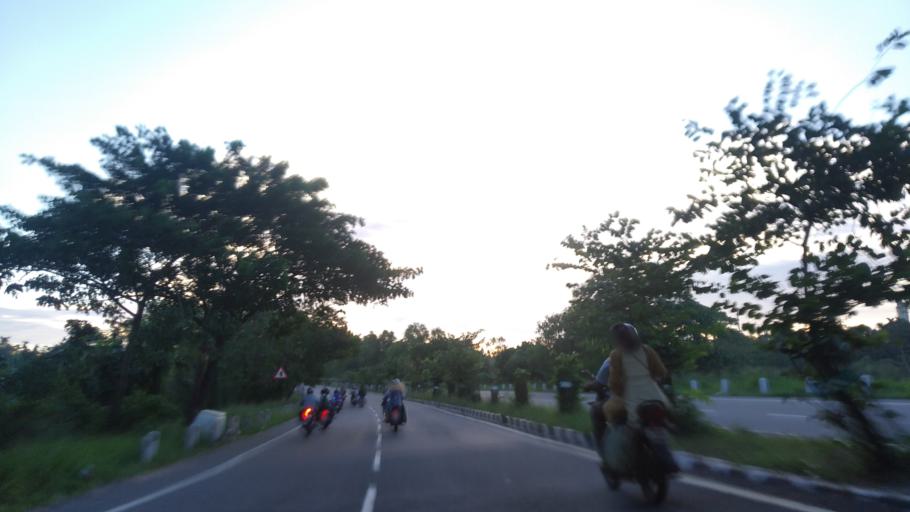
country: IN
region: Kerala
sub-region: Ernakulam
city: Elur
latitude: 10.0692
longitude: 76.3024
